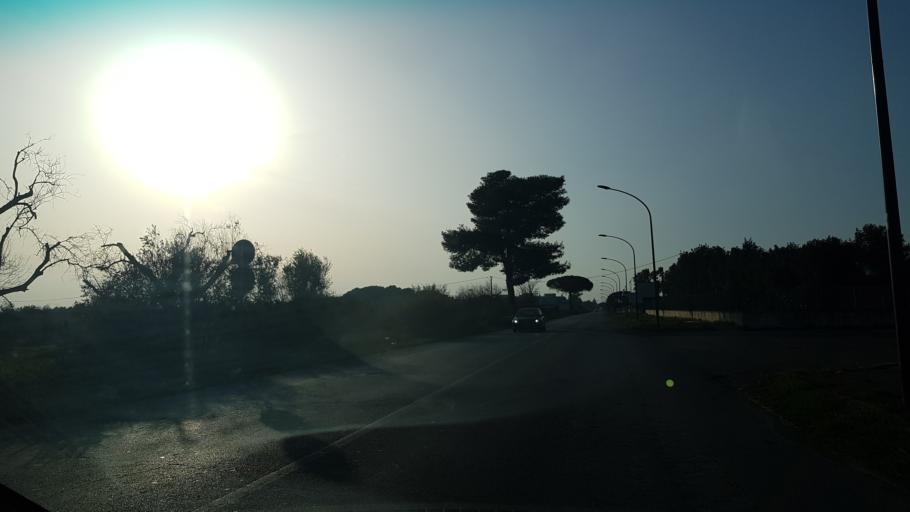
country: IT
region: Apulia
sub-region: Provincia di Lecce
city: Novoli
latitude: 40.3956
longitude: 18.0426
